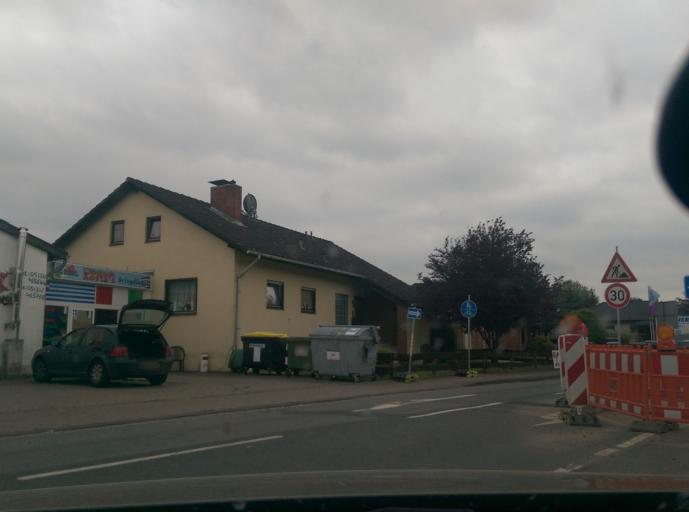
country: DE
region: Lower Saxony
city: Garbsen-Mitte
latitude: 52.4469
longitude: 9.6073
